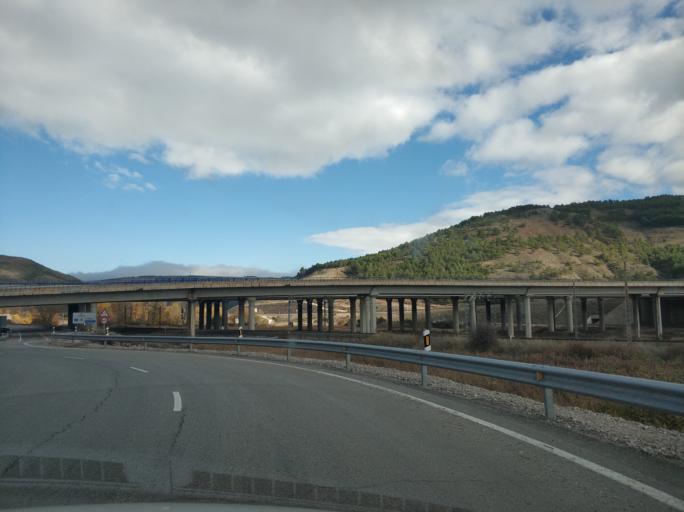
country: ES
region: Castille and Leon
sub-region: Provincia de Soria
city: Medinaceli
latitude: 41.1694
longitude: -2.4206
